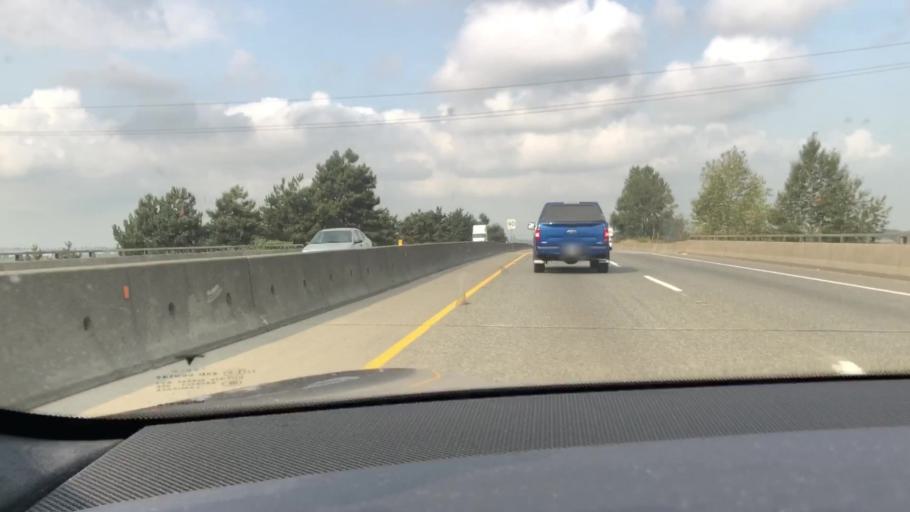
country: CA
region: British Columbia
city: New Westminster
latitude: 49.1705
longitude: -122.9989
